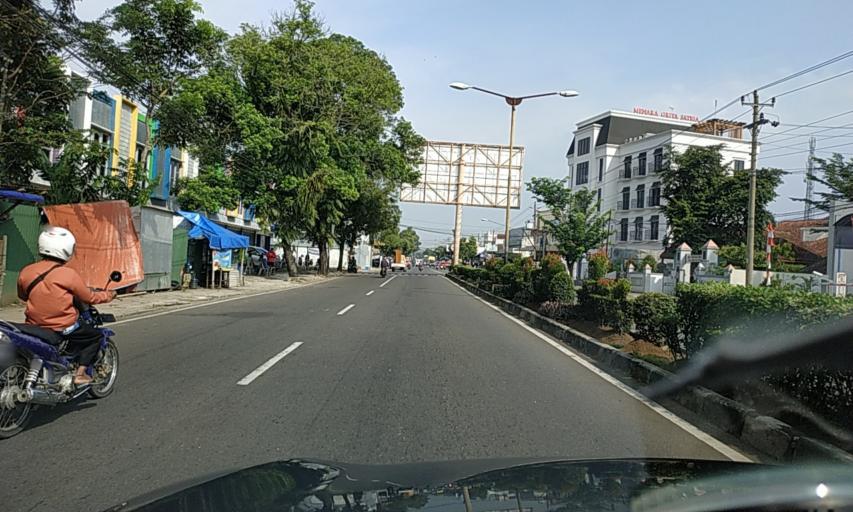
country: ID
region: Central Java
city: Purwokerto
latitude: -7.4209
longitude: 109.2027
